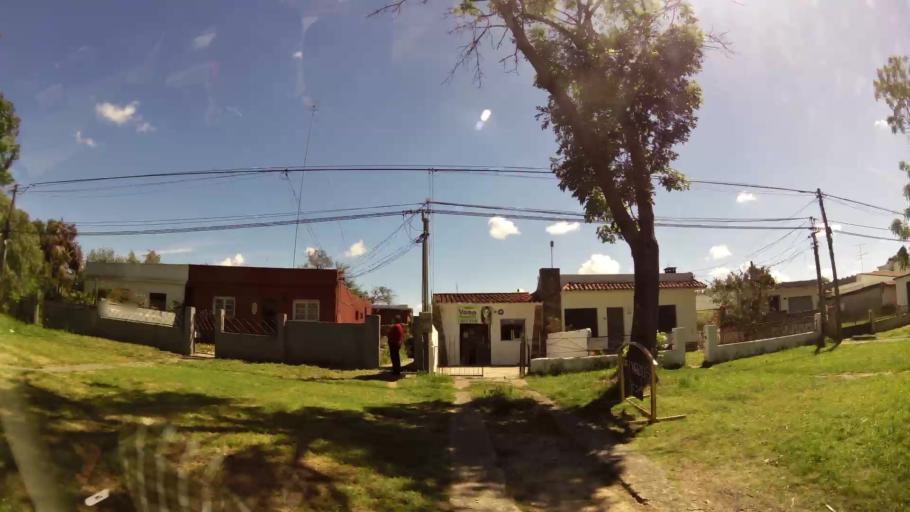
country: UY
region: Canelones
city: Paso de Carrasco
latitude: -34.8434
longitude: -56.1220
